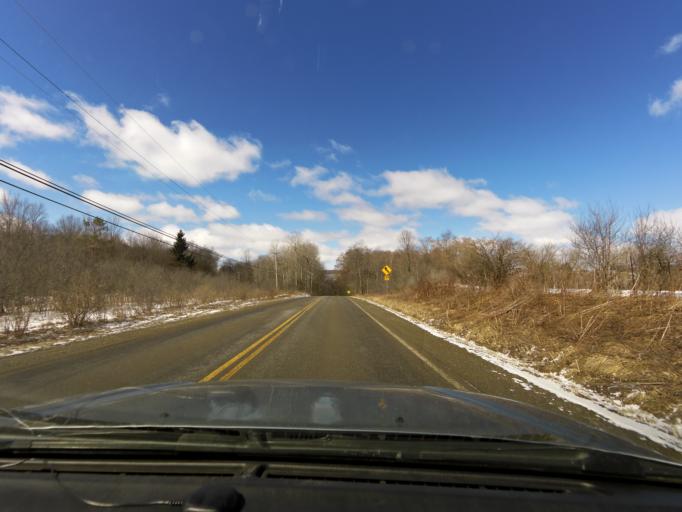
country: US
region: New York
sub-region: Cattaraugus County
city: Franklinville
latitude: 42.3437
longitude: -78.4348
